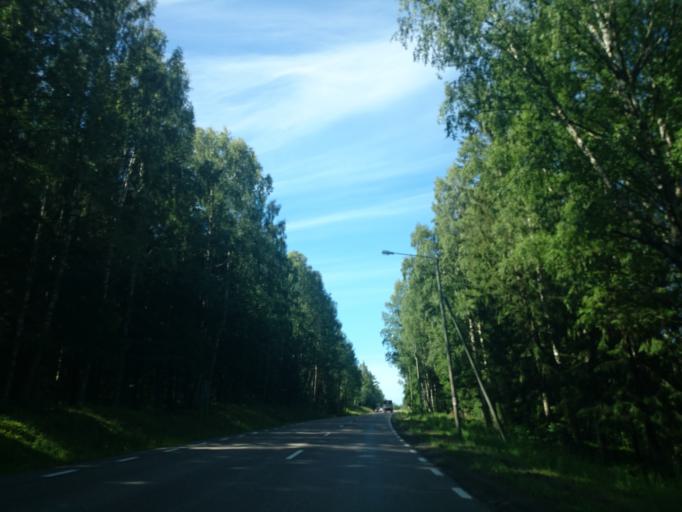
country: SE
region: Vaesternorrland
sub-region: Sundsvalls Kommun
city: Vi
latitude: 62.3938
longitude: 17.1935
